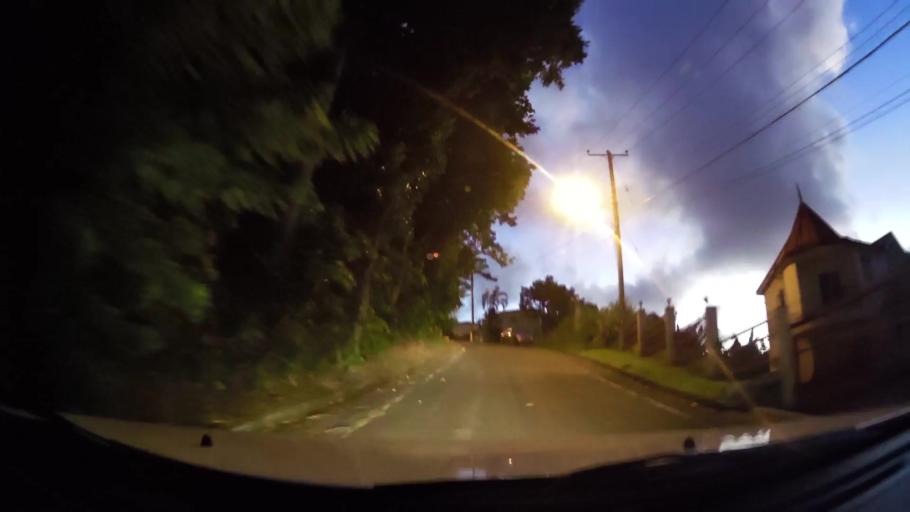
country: LC
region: Castries Quarter
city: Bisee
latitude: 14.0281
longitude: -60.9463
